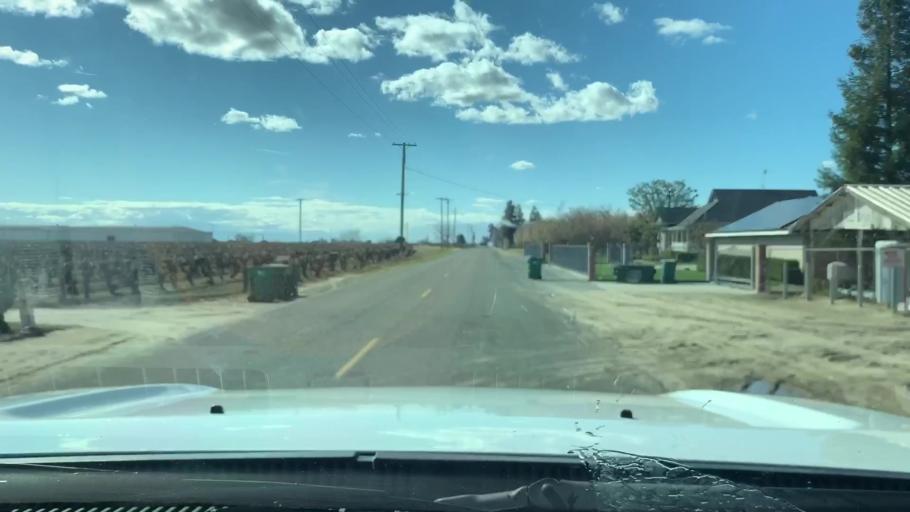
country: US
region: California
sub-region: Fresno County
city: Fowler
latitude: 36.5619
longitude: -119.7335
